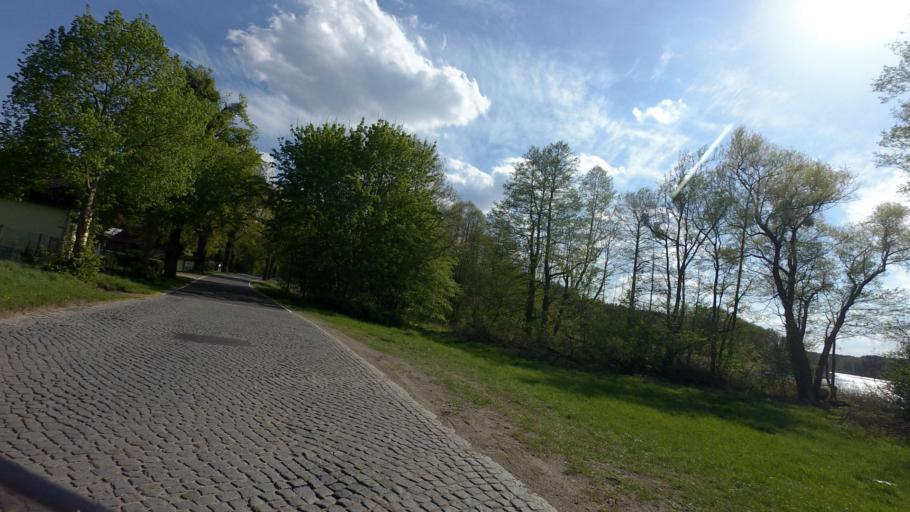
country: DE
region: Brandenburg
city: Milmersdorf
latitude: 53.0479
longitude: 13.6029
